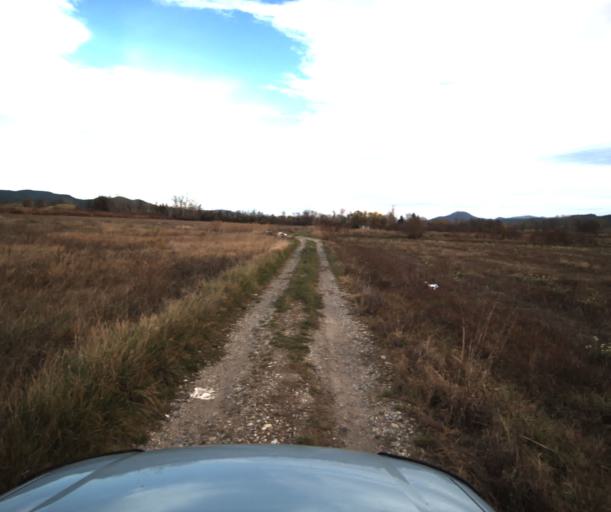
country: FR
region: Provence-Alpes-Cote d'Azur
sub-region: Departement des Bouches-du-Rhone
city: Meyrargues
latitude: 43.6667
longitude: 5.5183
